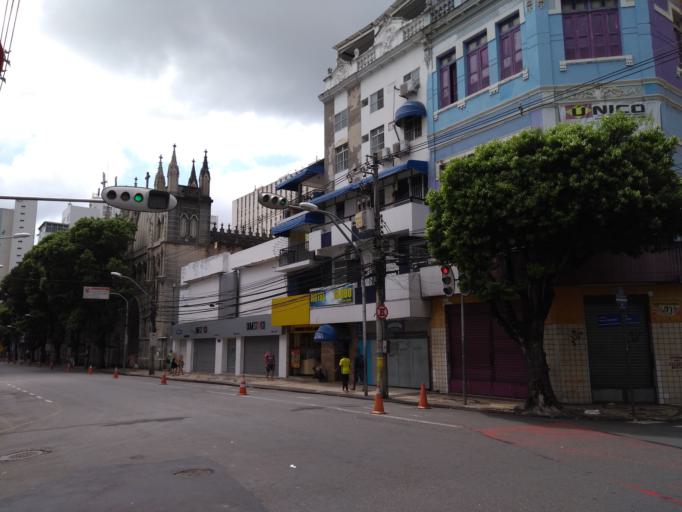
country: BR
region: Bahia
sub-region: Salvador
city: Salvador
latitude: -12.9857
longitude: -38.5196
